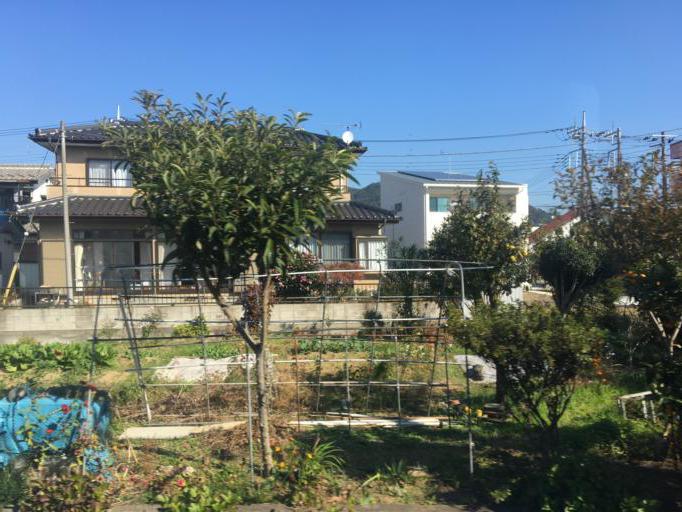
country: JP
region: Tochigi
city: Ashikaga
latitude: 36.3507
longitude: 139.4068
